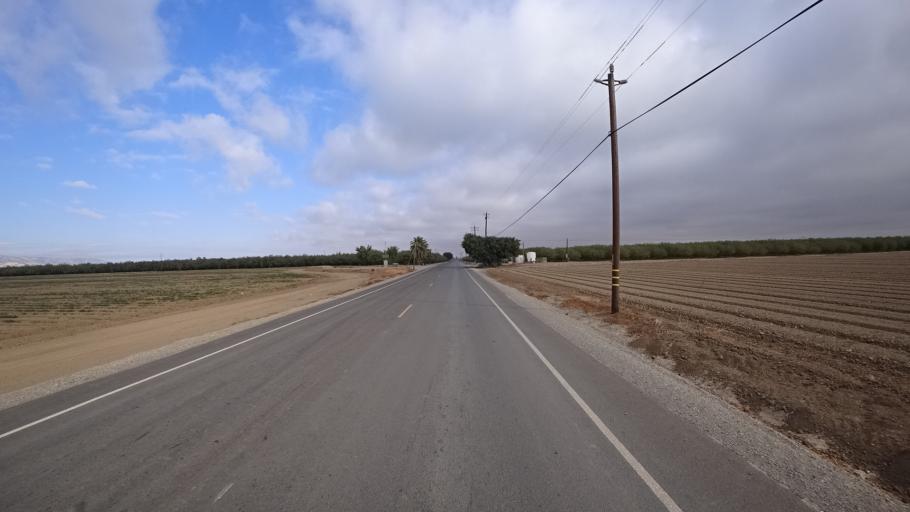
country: US
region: California
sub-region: Yolo County
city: Esparto
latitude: 38.7221
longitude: -122.0086
